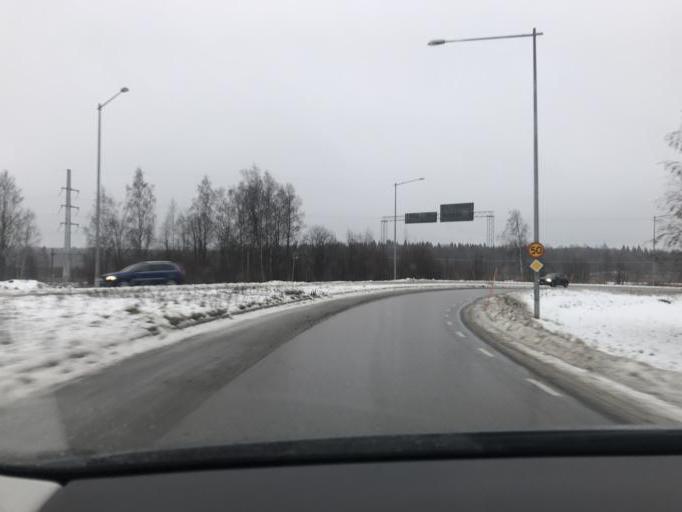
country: SE
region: Norrbotten
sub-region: Lulea Kommun
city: Bergnaset
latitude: 65.6145
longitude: 22.1019
